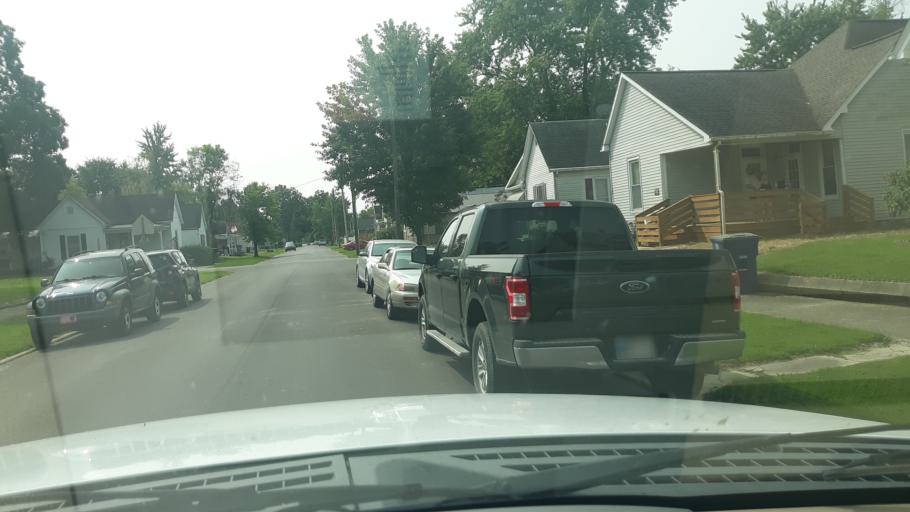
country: US
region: Indiana
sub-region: Gibson County
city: Princeton
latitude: 38.3505
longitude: -87.5627
